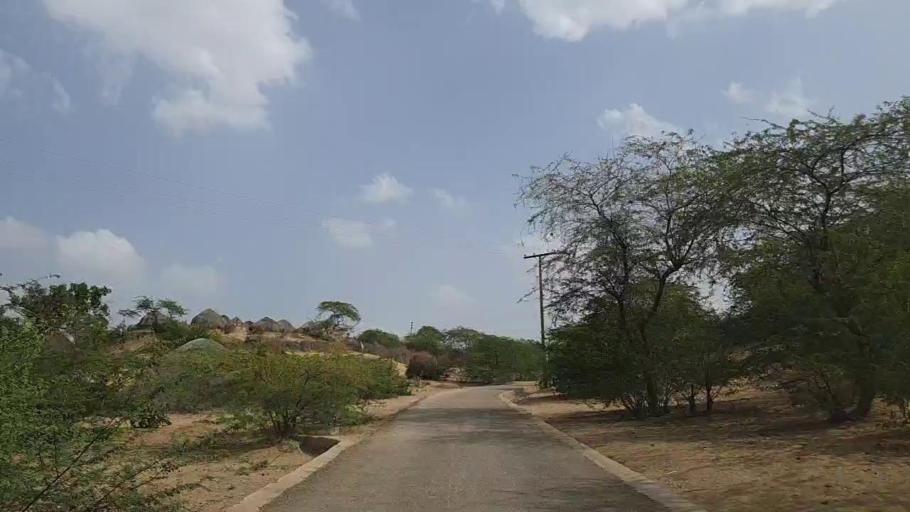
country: PK
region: Sindh
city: Islamkot
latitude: 24.8292
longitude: 70.1849
